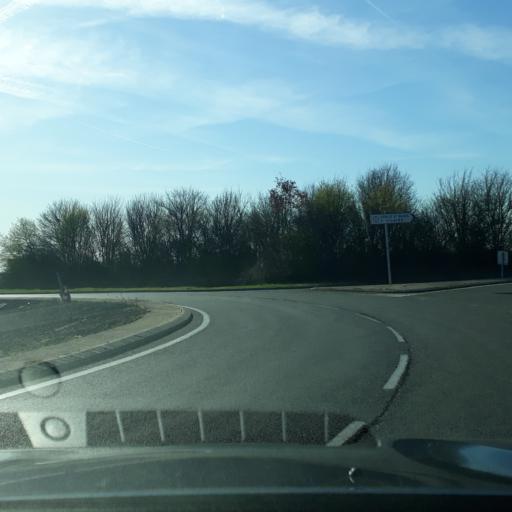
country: FR
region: Ile-de-France
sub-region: Departement de l'Essonne
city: Etampes
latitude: 48.4468
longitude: 2.1059
